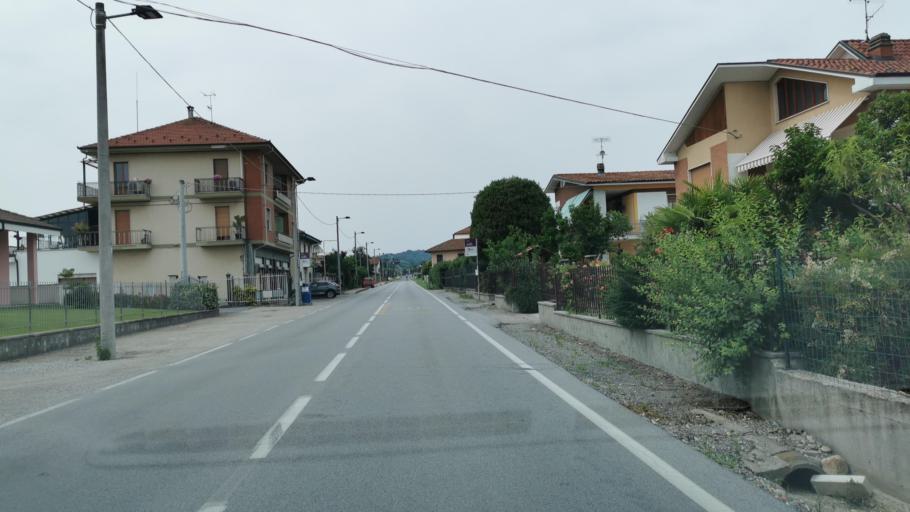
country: IT
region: Piedmont
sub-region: Provincia di Cuneo
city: Cinzano
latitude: 44.6893
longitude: 7.8941
